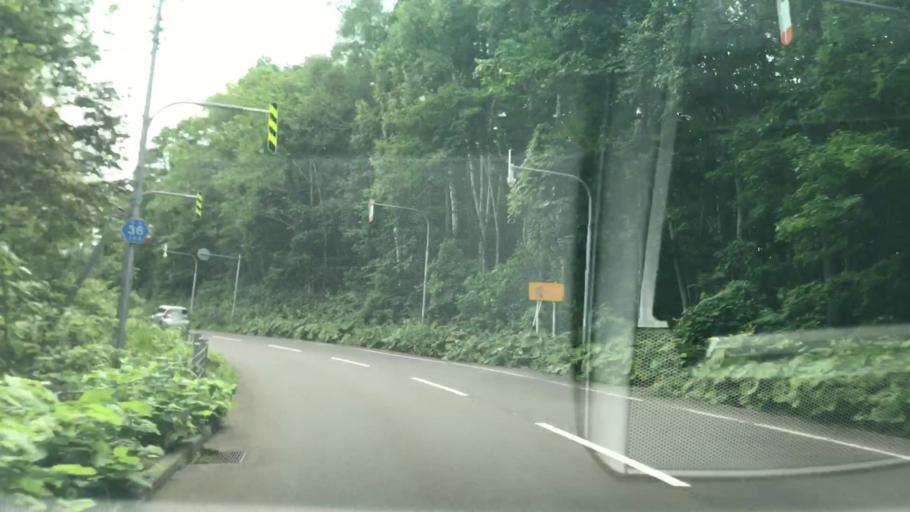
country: JP
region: Hokkaido
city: Yoichi
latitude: 43.1324
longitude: 140.8252
